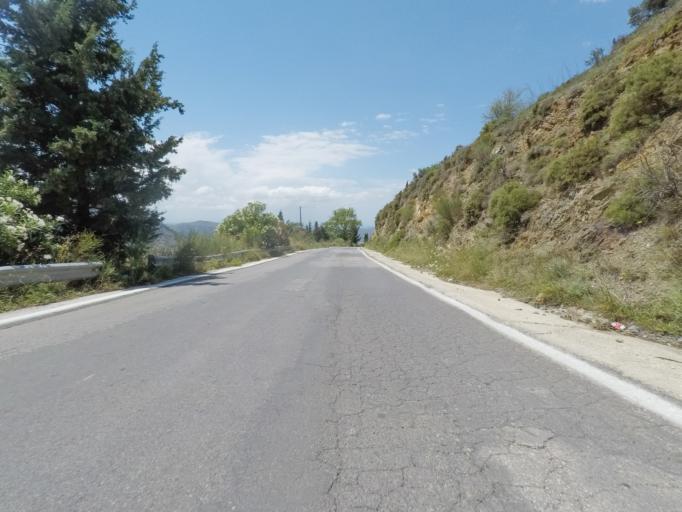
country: GR
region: Crete
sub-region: Nomos Irakleiou
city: Mokhos
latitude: 35.2139
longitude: 25.4605
